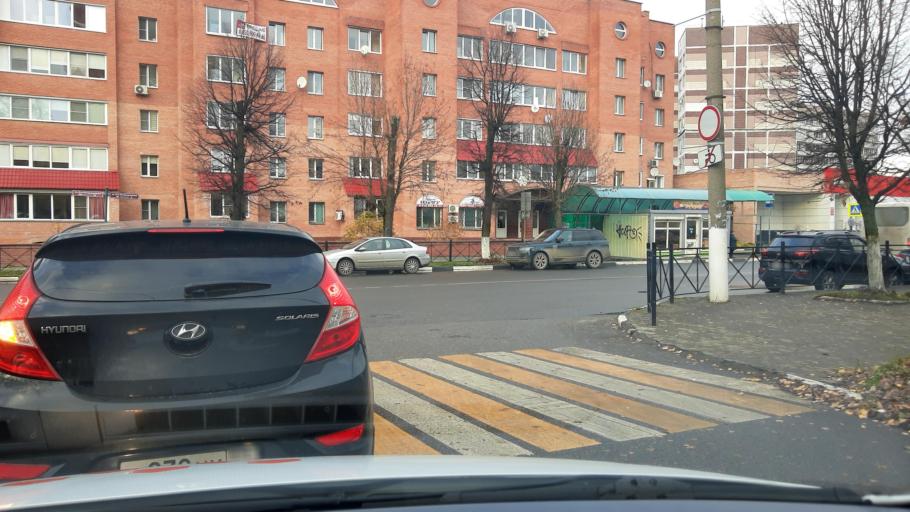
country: RU
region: Moskovskaya
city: Noginsk
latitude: 55.8521
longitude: 38.4306
